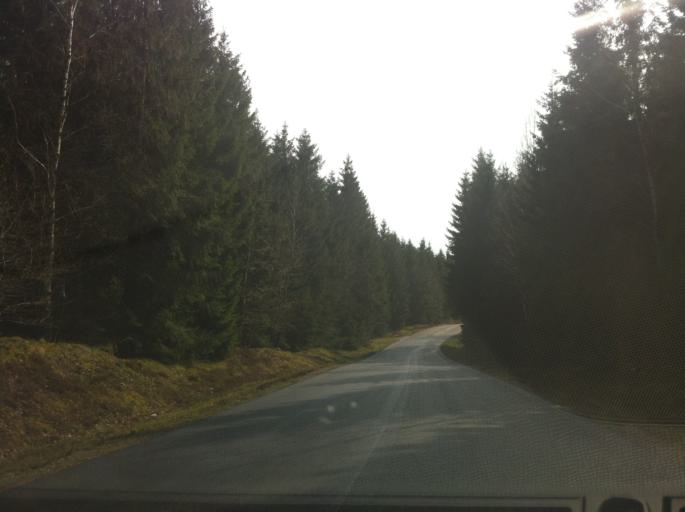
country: SE
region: Skane
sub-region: Perstorps Kommun
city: Perstorp
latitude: 56.1039
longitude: 13.4126
